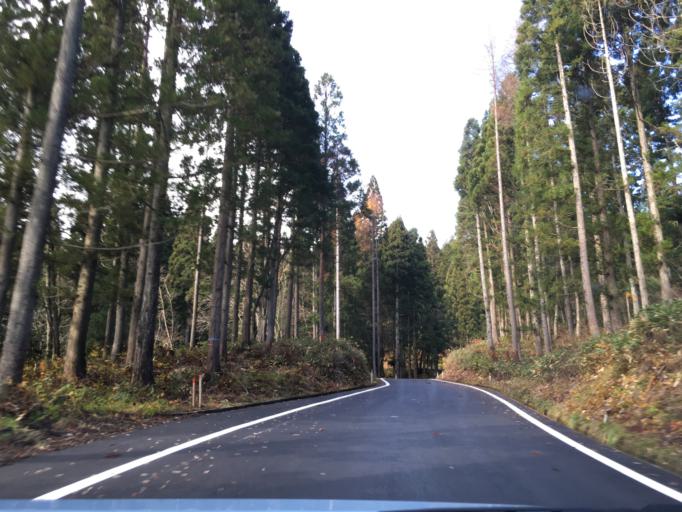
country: JP
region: Fukushima
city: Inawashiro
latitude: 37.4584
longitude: 139.9995
